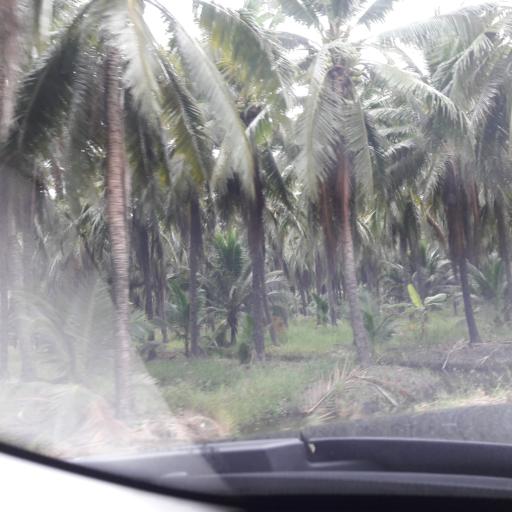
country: TH
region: Ratchaburi
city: Damnoen Saduak
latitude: 13.5716
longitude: 99.9415
